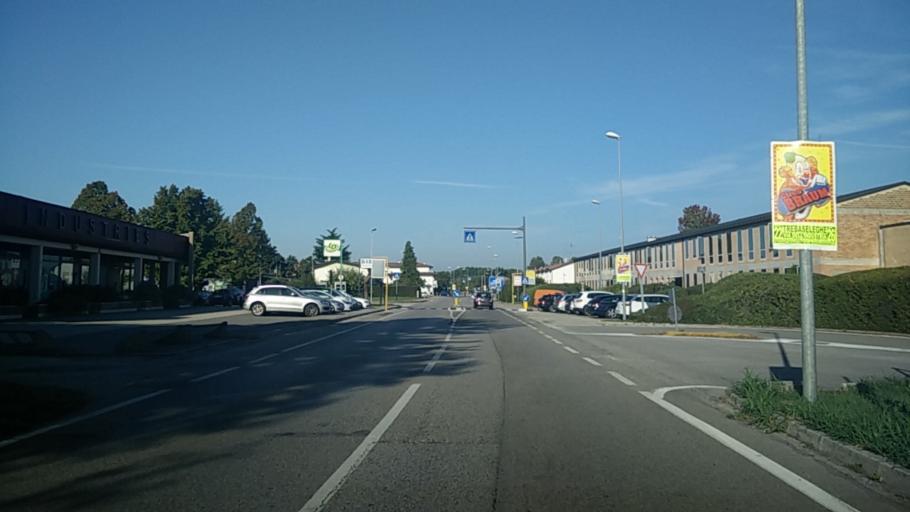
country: IT
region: Veneto
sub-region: Provincia di Padova
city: Trebaseleghe
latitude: 45.5865
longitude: 12.0555
